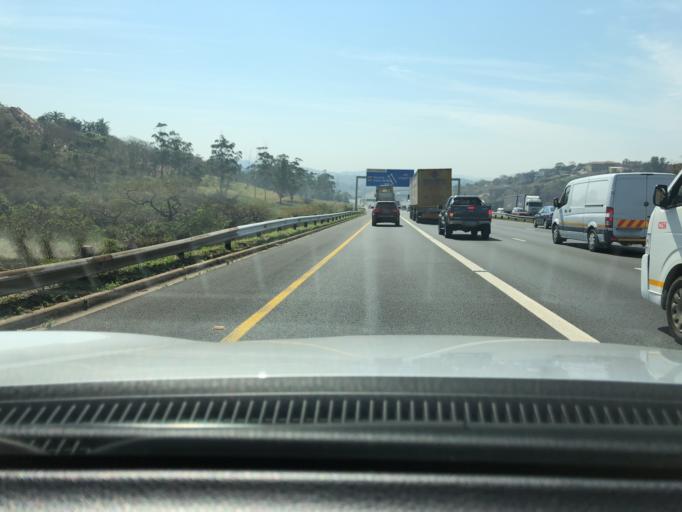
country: ZA
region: KwaZulu-Natal
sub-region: eThekwini Metropolitan Municipality
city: Berea
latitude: -29.8143
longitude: 30.9738
